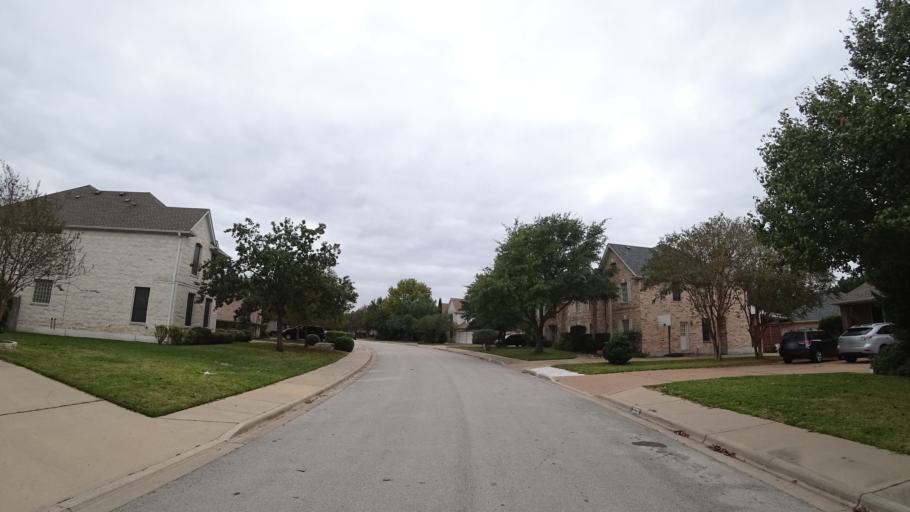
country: US
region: Texas
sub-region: Travis County
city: Bee Cave
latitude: 30.3138
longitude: -97.9259
